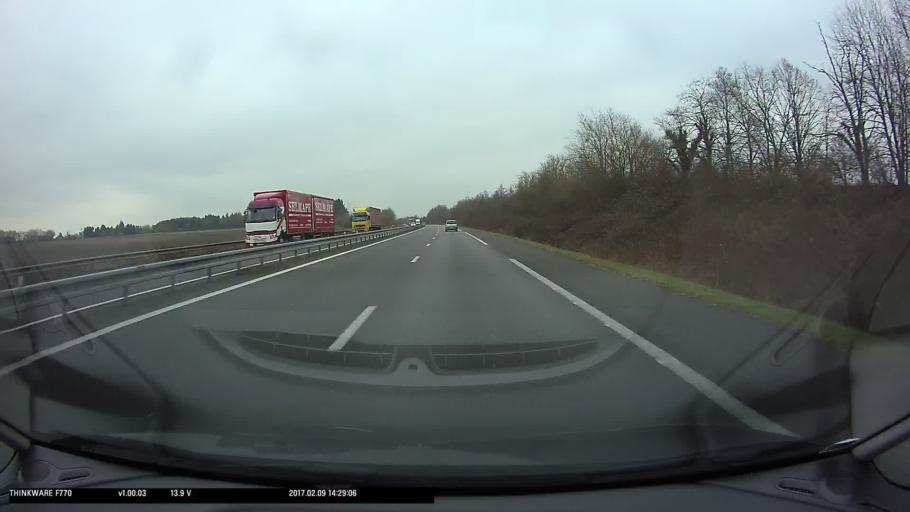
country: FR
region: Centre
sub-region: Departement du Cher
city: Mehun-sur-Yevre
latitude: 47.1193
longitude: 2.1944
